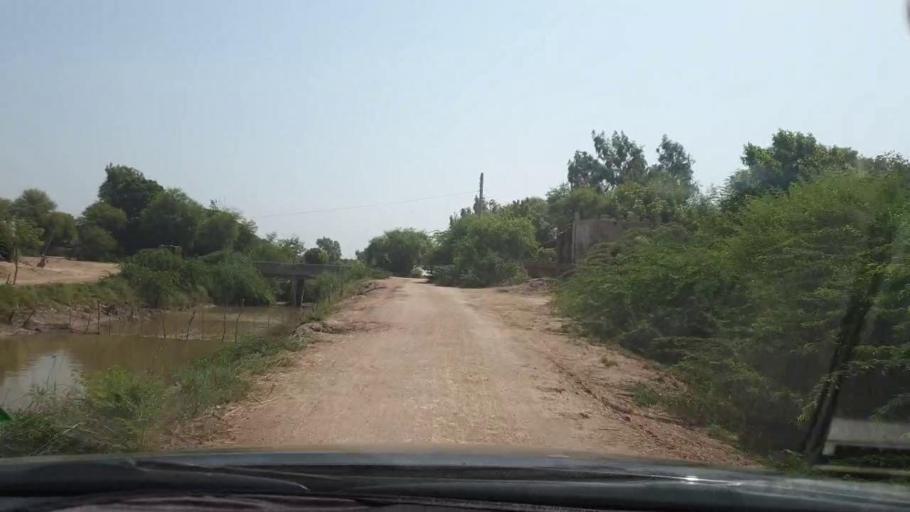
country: PK
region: Sindh
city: Tando Bago
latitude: 24.7841
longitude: 69.1268
